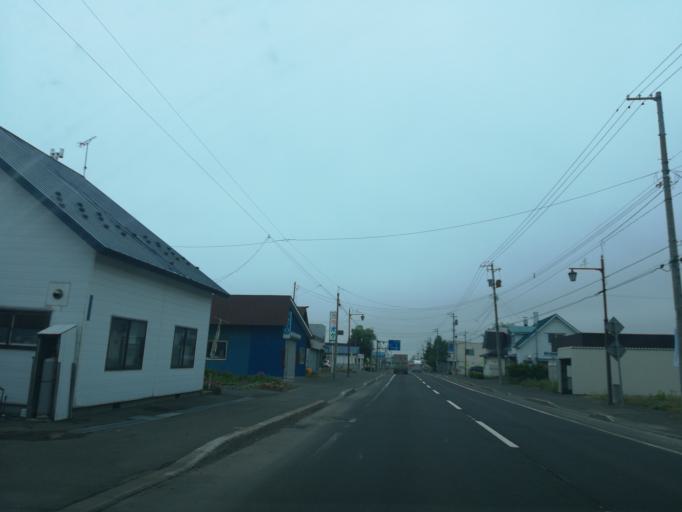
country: JP
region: Hokkaido
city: Ebetsu
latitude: 43.0718
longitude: 141.6475
